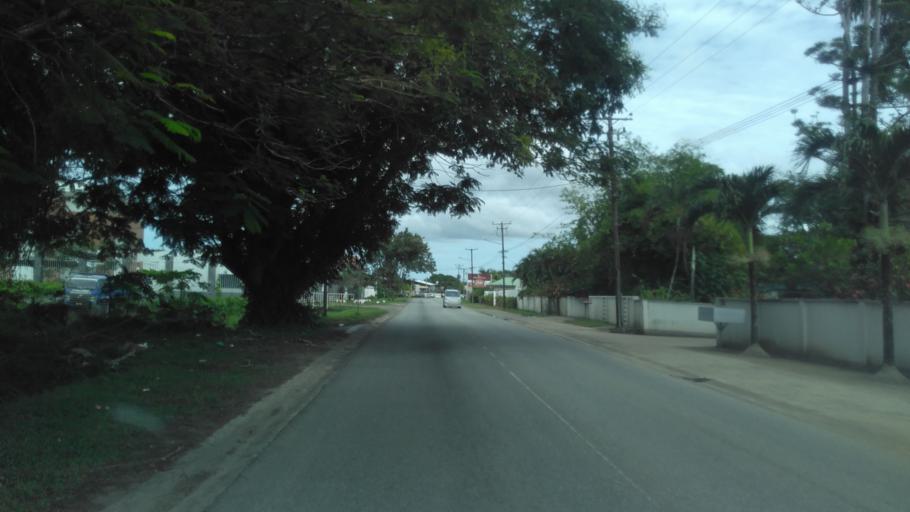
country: SR
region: Paramaribo
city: Paramaribo
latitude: 5.8385
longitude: -55.1213
